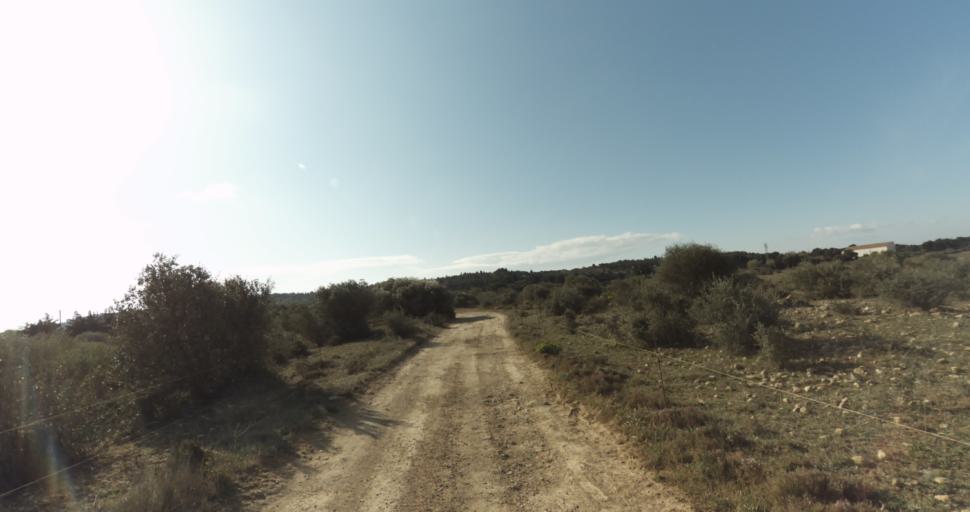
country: FR
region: Languedoc-Roussillon
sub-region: Departement de l'Aude
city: Leucate
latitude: 42.9370
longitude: 3.0131
